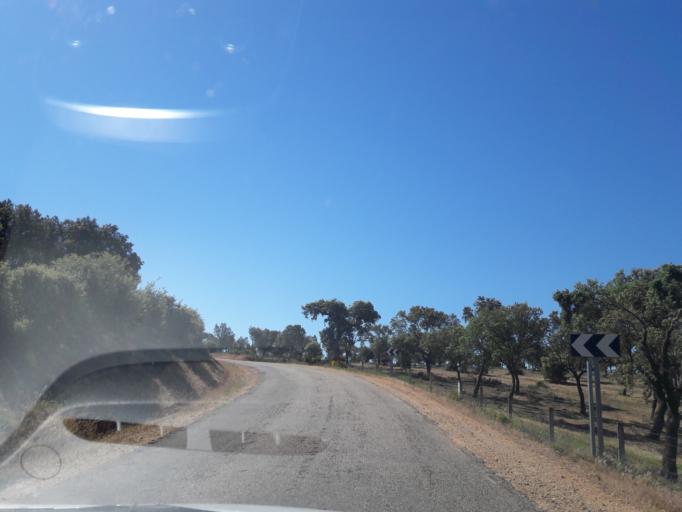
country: ES
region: Castille and Leon
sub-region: Provincia de Salamanca
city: Vega de Tirados
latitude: 41.0541
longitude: -5.8907
